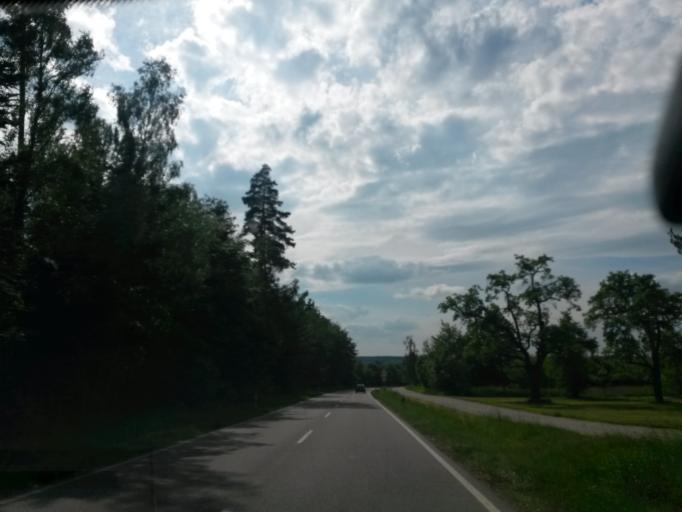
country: DE
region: Baden-Wuerttemberg
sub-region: Karlsruhe Region
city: Calw
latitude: 48.7439
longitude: 8.7603
